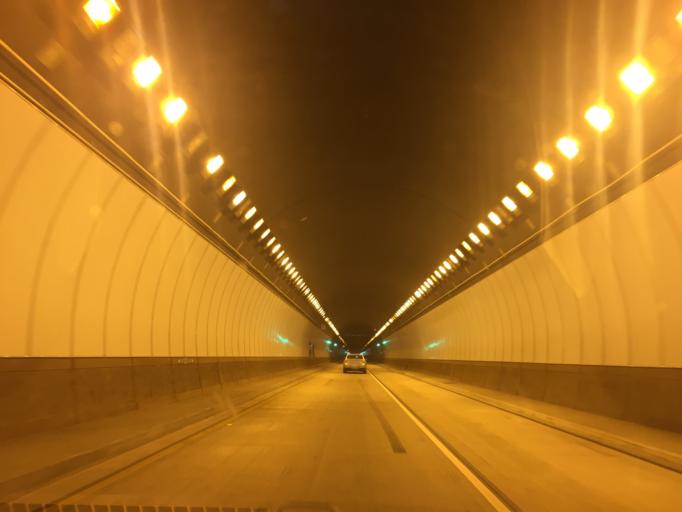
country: US
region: California
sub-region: San Mateo County
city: Pacifica
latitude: 37.5822
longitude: -122.5101
